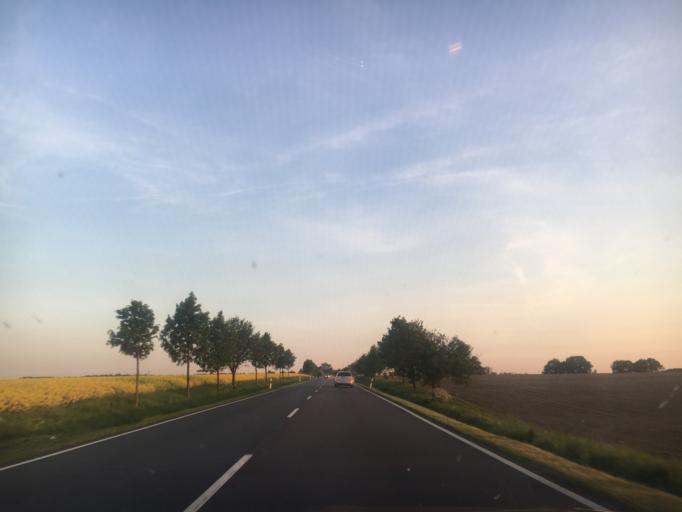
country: DE
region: Thuringia
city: Hirschfeld
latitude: 50.9870
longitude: 12.1385
